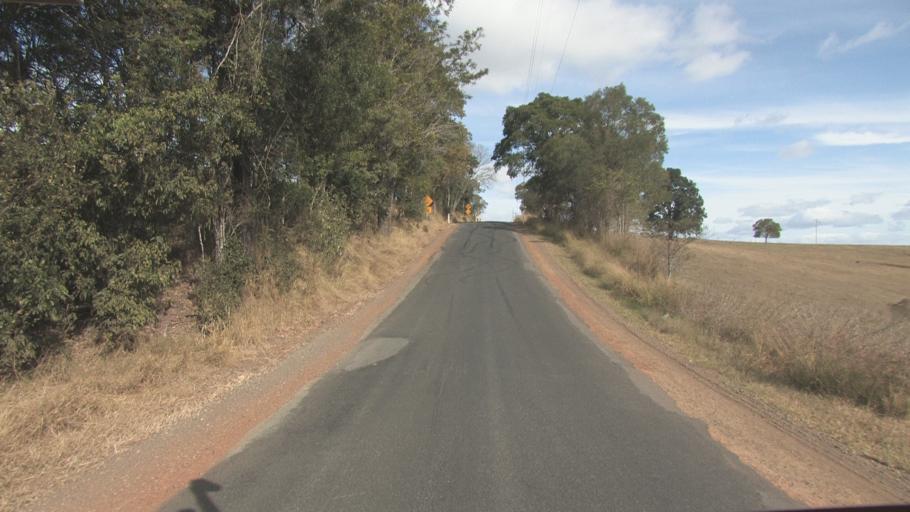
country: AU
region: Queensland
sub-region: Logan
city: Cedar Vale
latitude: -27.9028
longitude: 153.0149
